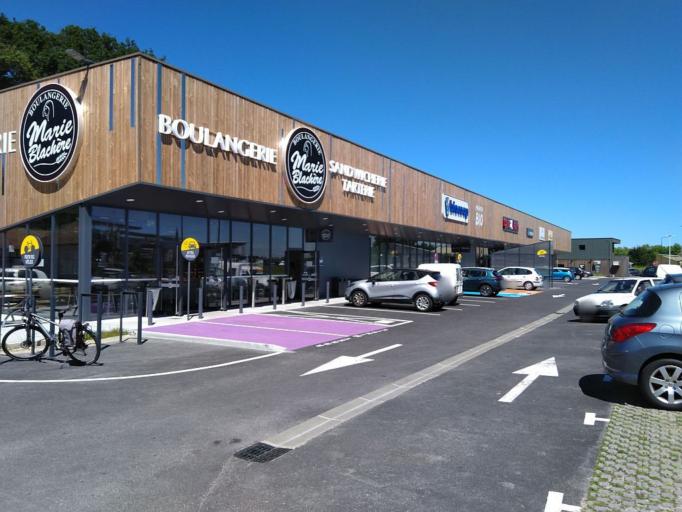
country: FR
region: Aquitaine
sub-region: Departement des Landes
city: Saint-Paul-les-Dax
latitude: 43.7321
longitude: -1.0414
